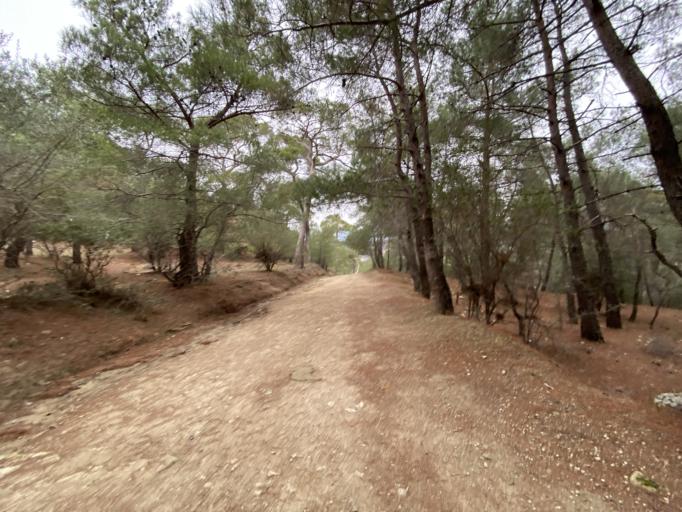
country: TR
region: Canakkale
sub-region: Merkez
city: Kucukkuyu
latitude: 39.5642
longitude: 26.6166
